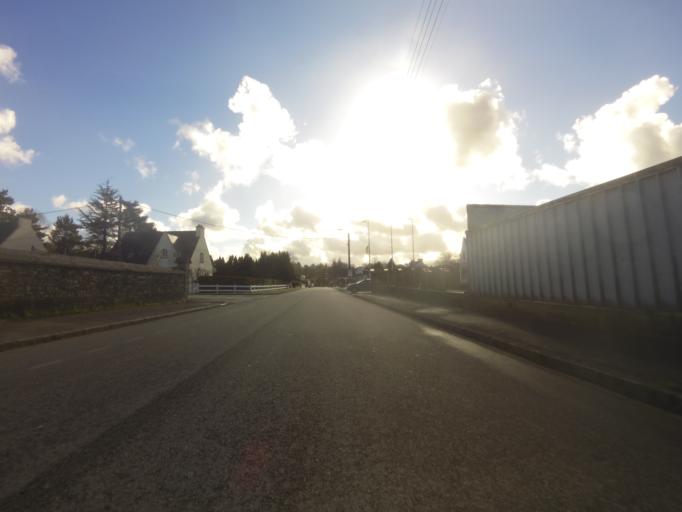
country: FR
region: Brittany
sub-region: Departement du Morbihan
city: Gourin
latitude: 48.1433
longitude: -3.6162
